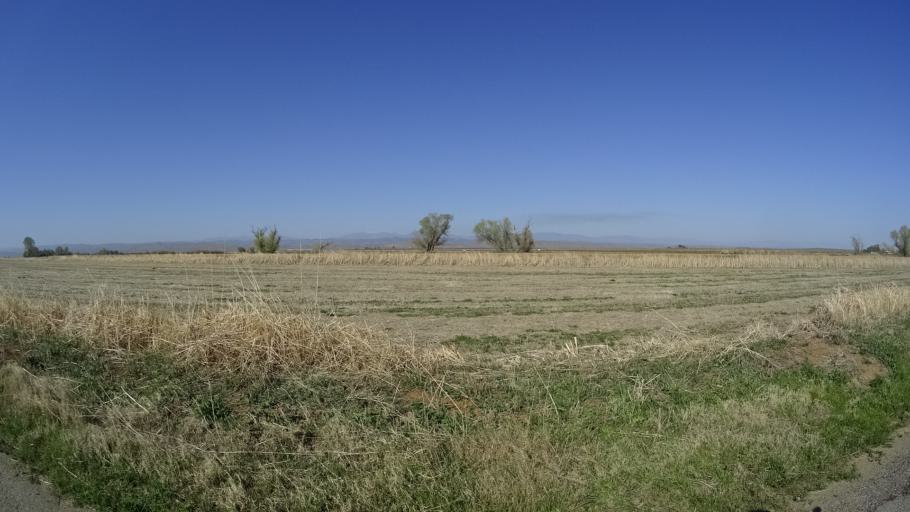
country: US
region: California
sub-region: Glenn County
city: Willows
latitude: 39.4397
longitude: -122.2303
